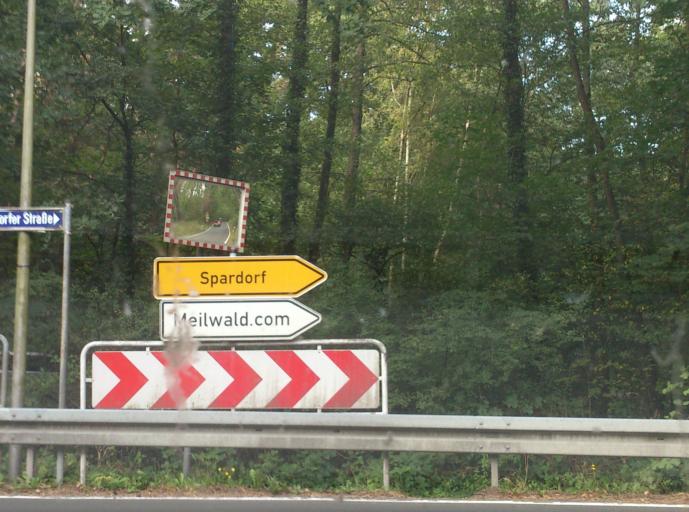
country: DE
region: Bavaria
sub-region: Regierungsbezirk Mittelfranken
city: Buckenhof
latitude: 49.6048
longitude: 11.0361
